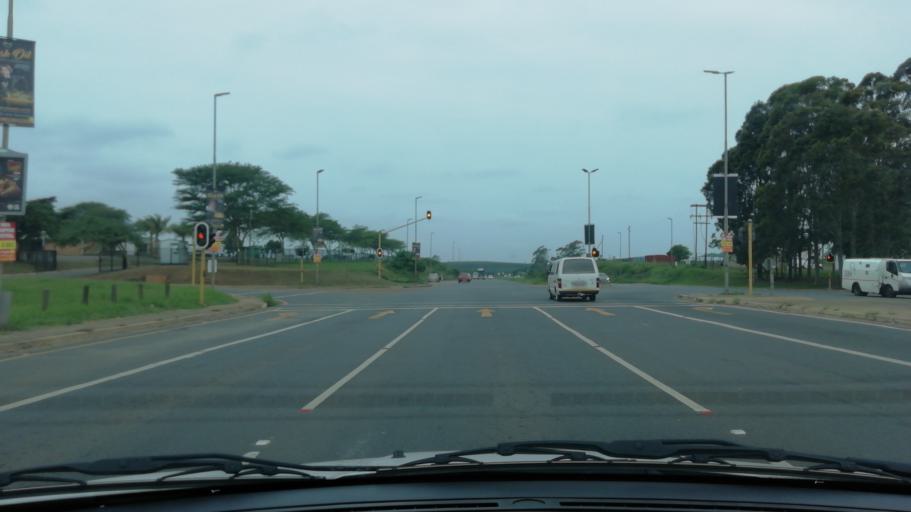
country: ZA
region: KwaZulu-Natal
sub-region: uThungulu District Municipality
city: Empangeni
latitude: -28.7669
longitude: 31.9142
